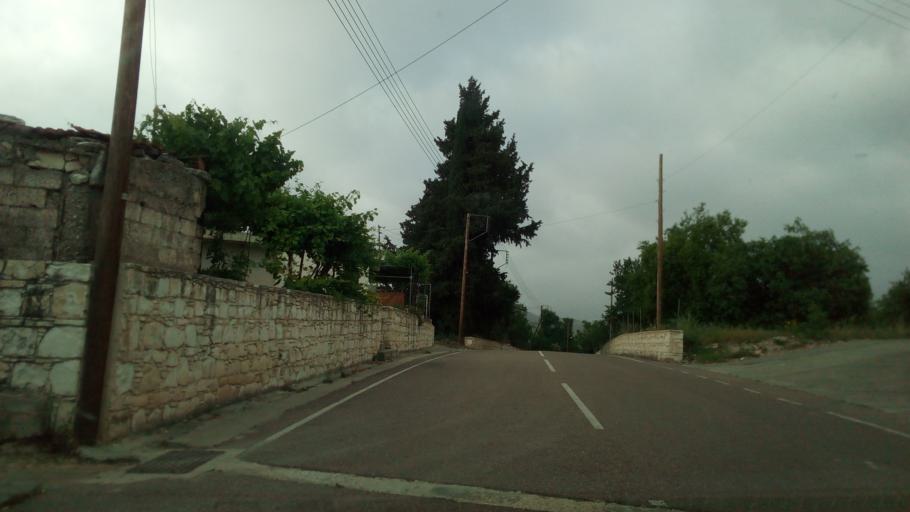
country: CY
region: Limassol
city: Pachna
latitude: 34.8374
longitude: 32.6886
